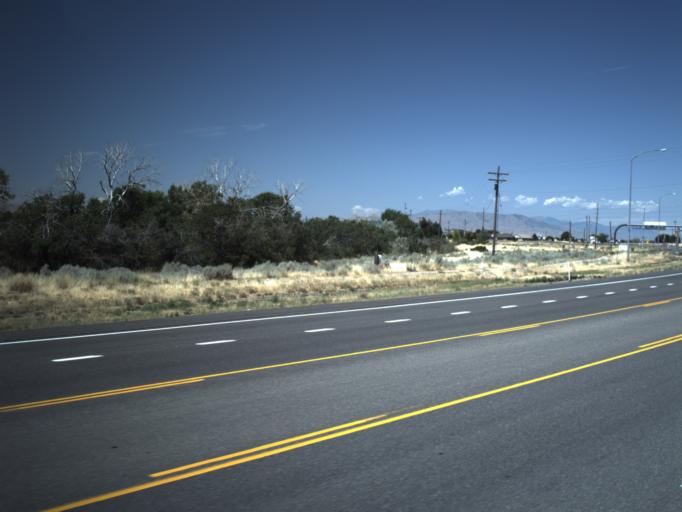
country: US
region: Utah
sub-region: Utah County
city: Mapleton
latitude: 40.0886
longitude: -111.5937
